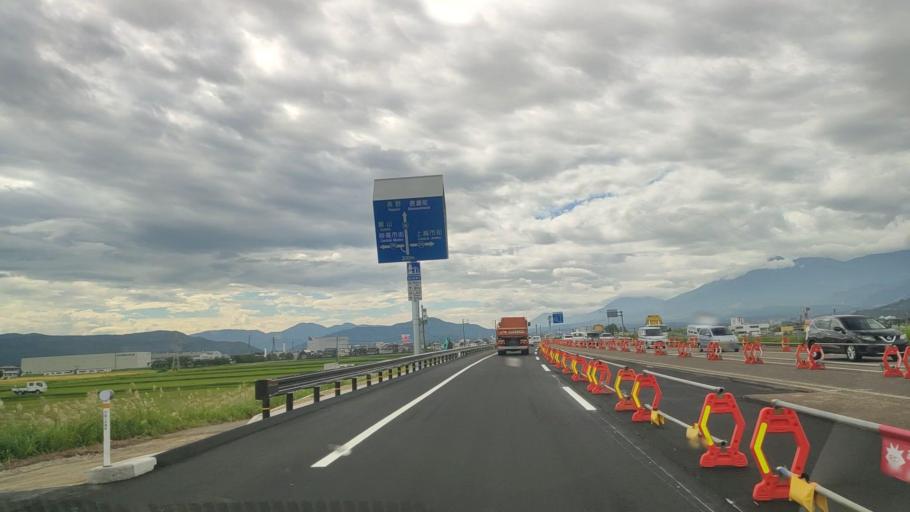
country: JP
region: Niigata
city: Arai
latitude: 37.0646
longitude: 138.2630
